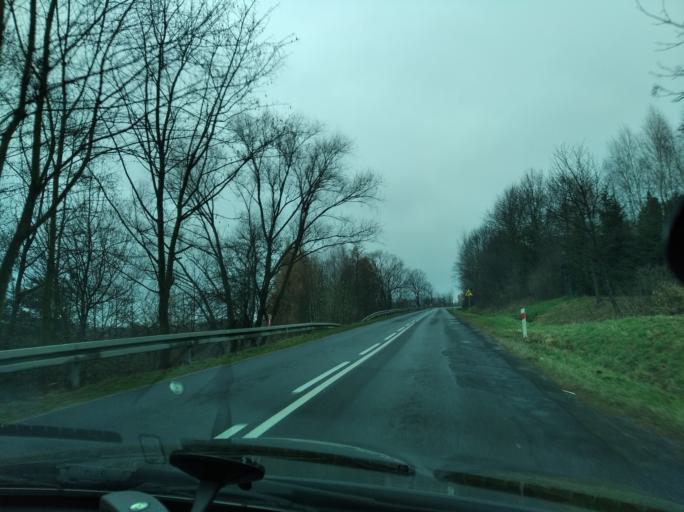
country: PL
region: Subcarpathian Voivodeship
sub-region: Powiat przeworski
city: Jawornik Polski
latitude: 49.8837
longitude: 22.2392
